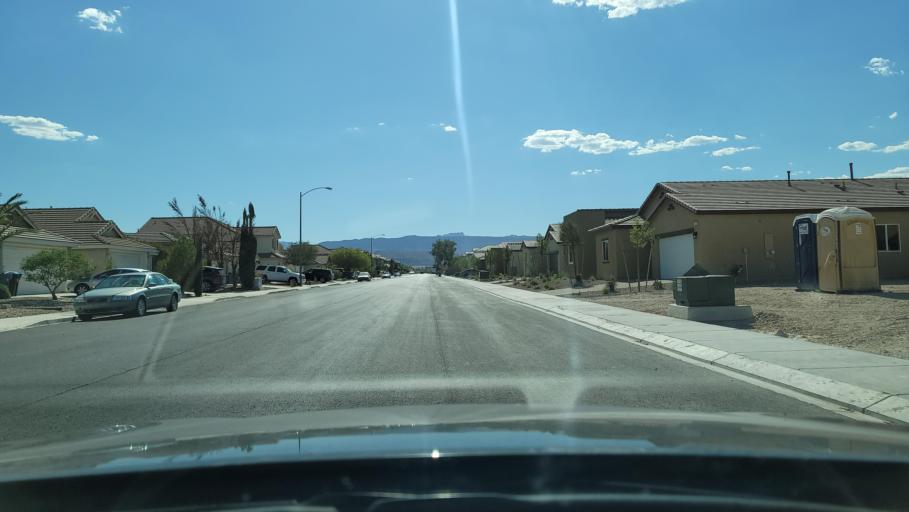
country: US
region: Nevada
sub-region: Clark County
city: Spring Valley
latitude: 36.0887
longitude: -115.2555
